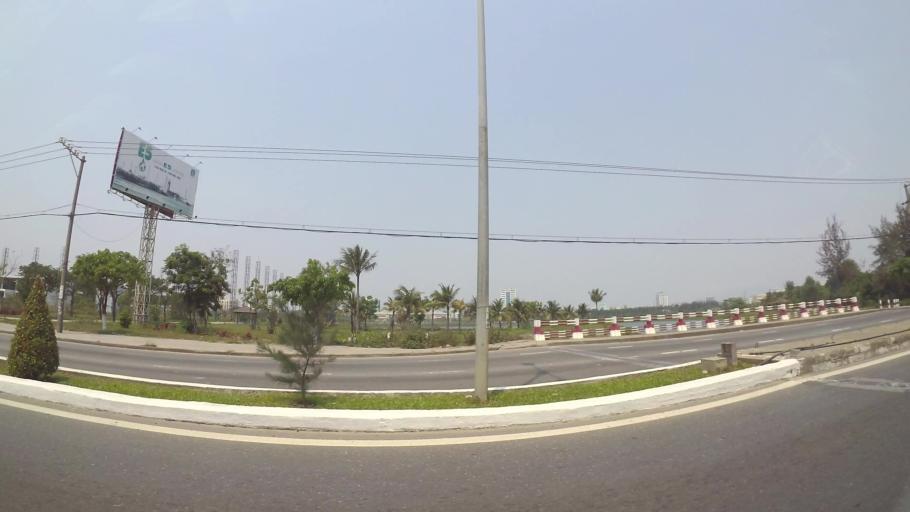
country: VN
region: Da Nang
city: Cam Le
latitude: 16.0246
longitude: 108.2180
